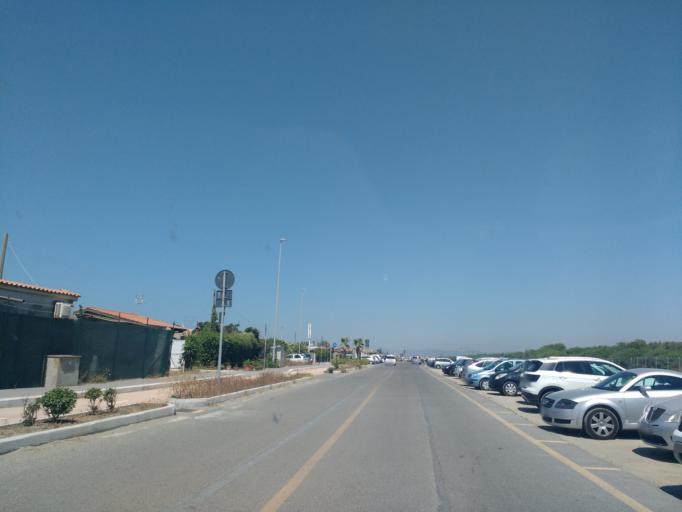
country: IT
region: Latium
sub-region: Citta metropolitana di Roma Capitale
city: Fregene
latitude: 41.8760
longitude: 12.1780
